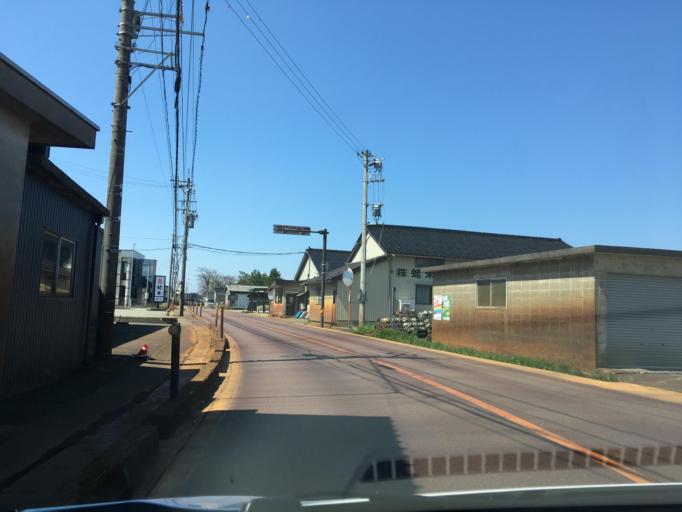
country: JP
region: Toyama
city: Kuragaki-kosugi
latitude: 36.7568
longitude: 137.1900
